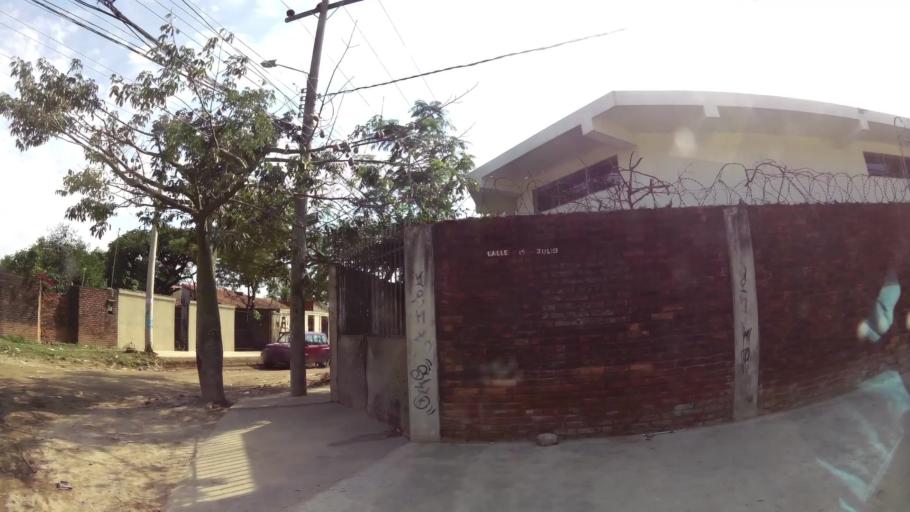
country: BO
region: Santa Cruz
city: Santa Cruz de la Sierra
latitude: -17.7264
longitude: -63.1550
